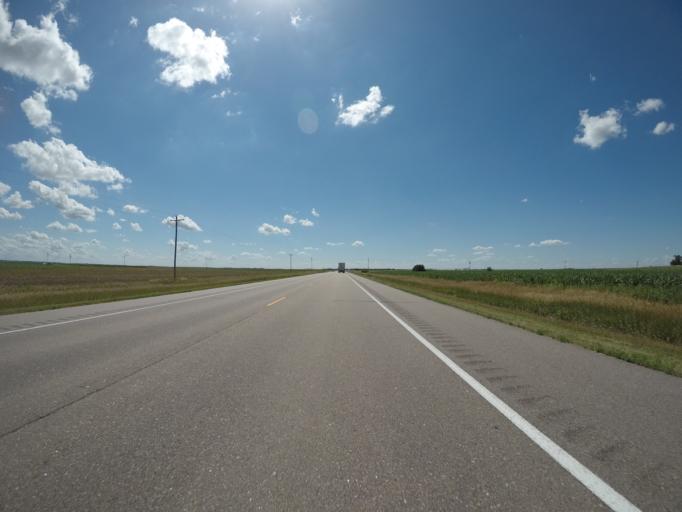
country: US
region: Nebraska
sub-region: Chase County
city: Imperial
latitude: 40.4943
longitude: -101.5878
